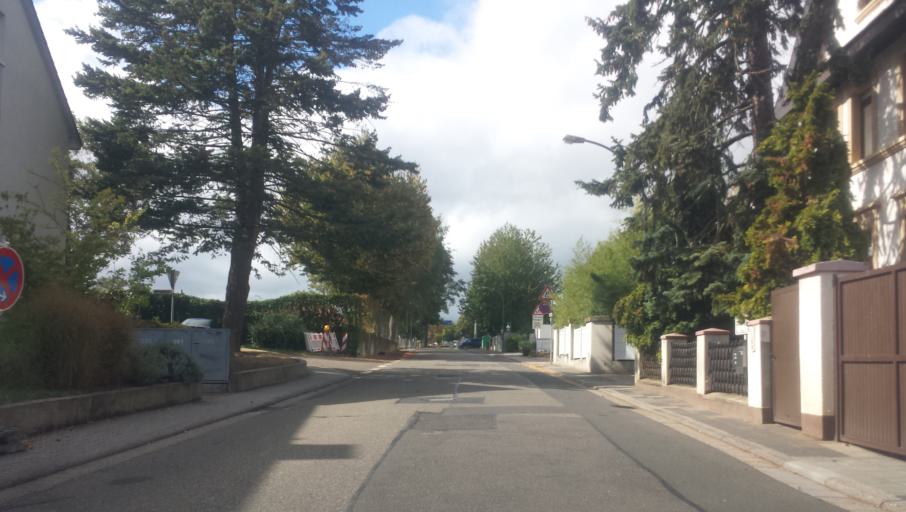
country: DE
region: Rheinland-Pfalz
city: Bochingen
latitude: 49.2226
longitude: 8.1062
